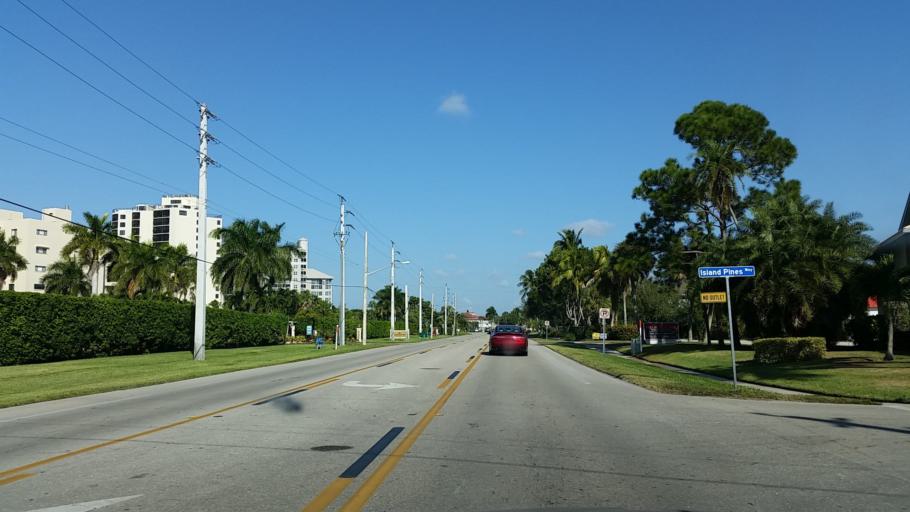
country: US
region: Florida
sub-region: Lee County
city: Fort Myers Beach
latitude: 26.4173
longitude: -81.9017
